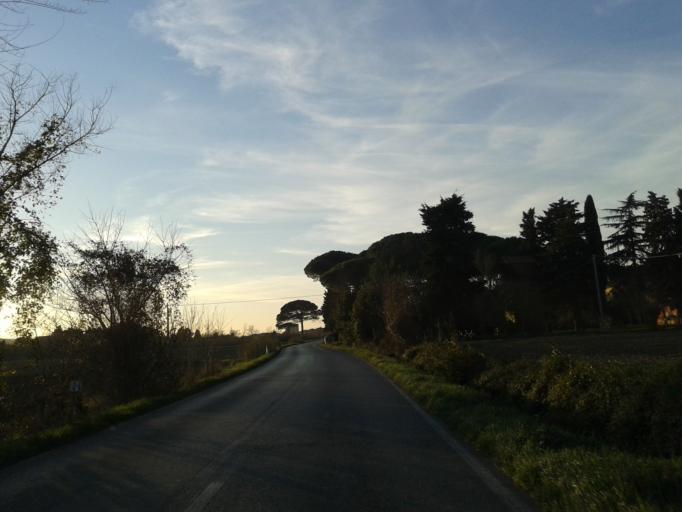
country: IT
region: Tuscany
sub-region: Provincia di Livorno
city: Guasticce
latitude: 43.5976
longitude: 10.4233
